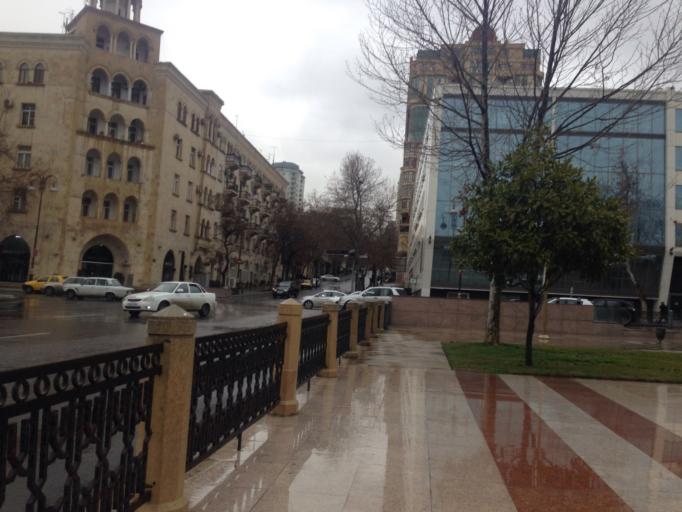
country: AZ
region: Baki
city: Baku
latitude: 40.3781
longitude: 49.8425
